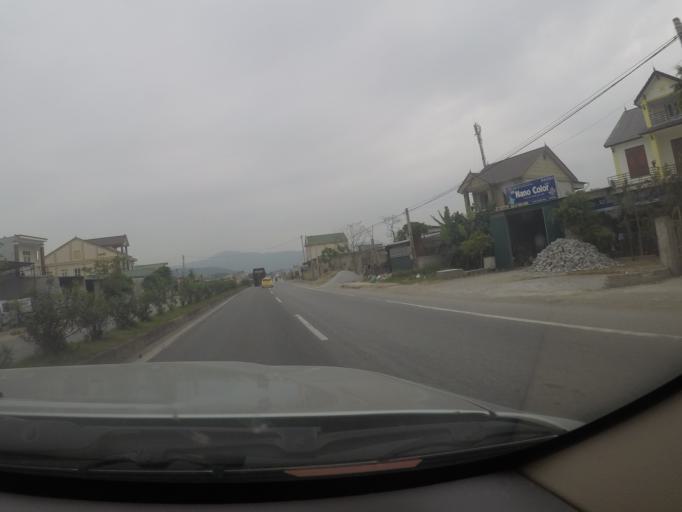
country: VN
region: Nghe An
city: Dien Chau
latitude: 18.9164
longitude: 105.6078
